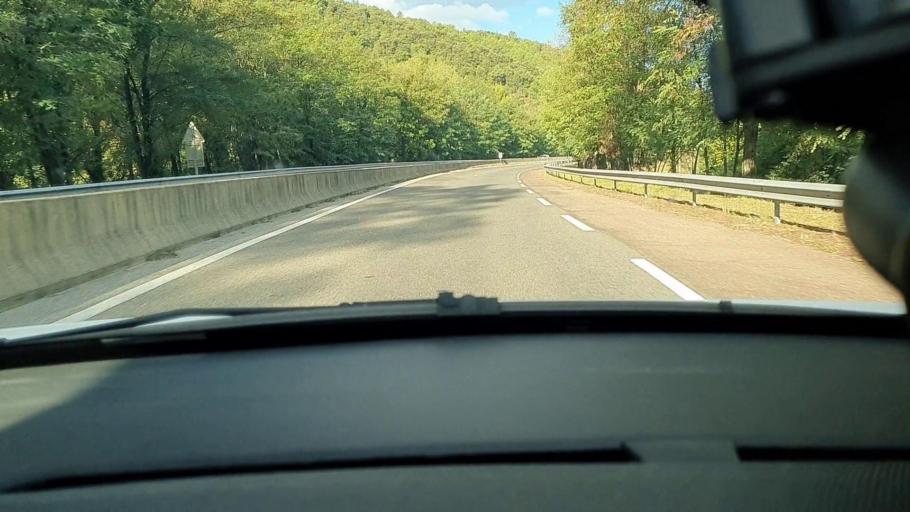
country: FR
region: Languedoc-Roussillon
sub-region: Departement du Gard
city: Molieres-sur-Ceze
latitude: 44.2626
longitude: 4.1578
